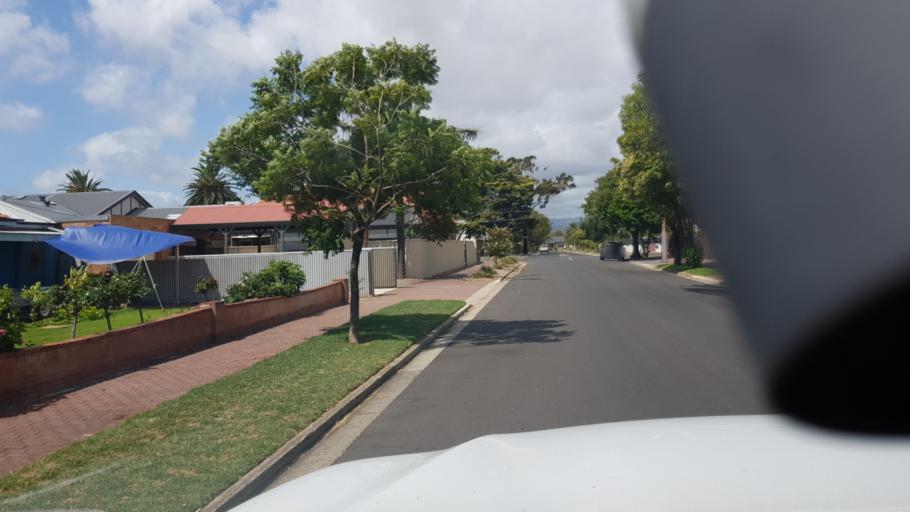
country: AU
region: South Australia
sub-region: Holdfast Bay
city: Glenelg East
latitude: -34.9846
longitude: 138.5258
